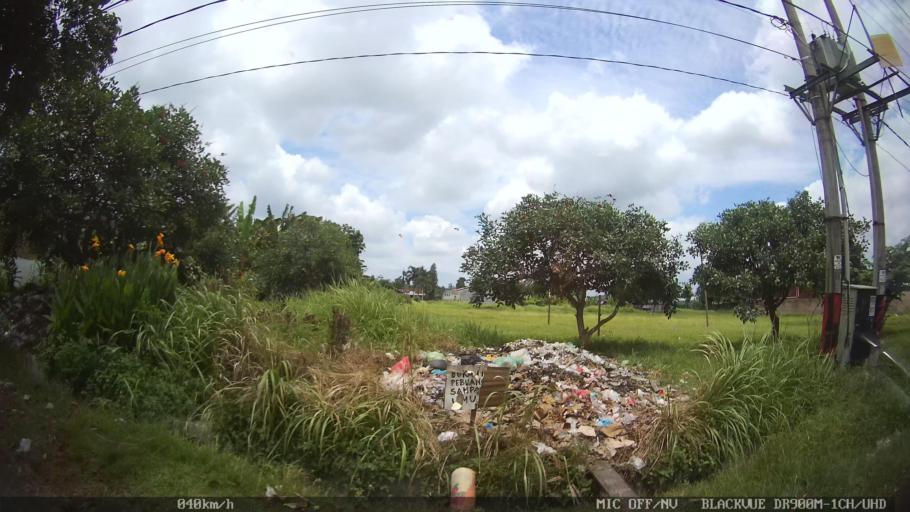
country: ID
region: North Sumatra
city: Medan
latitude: 3.6214
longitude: 98.7484
